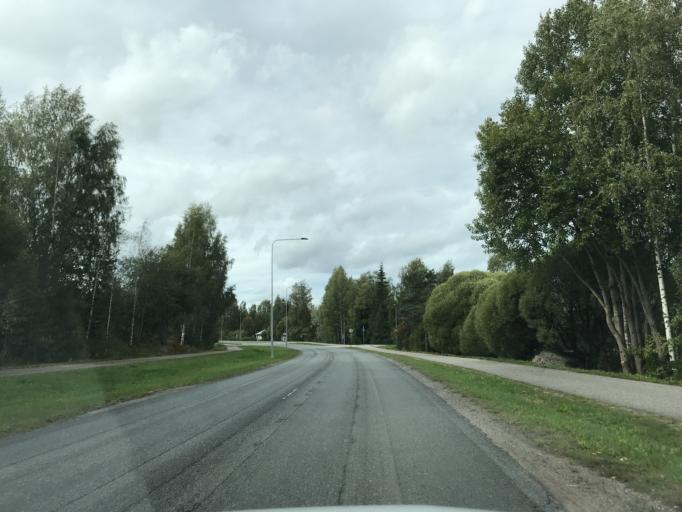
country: FI
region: Paijanne Tavastia
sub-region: Lahti
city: Lahti
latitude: 61.0117
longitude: 25.7915
